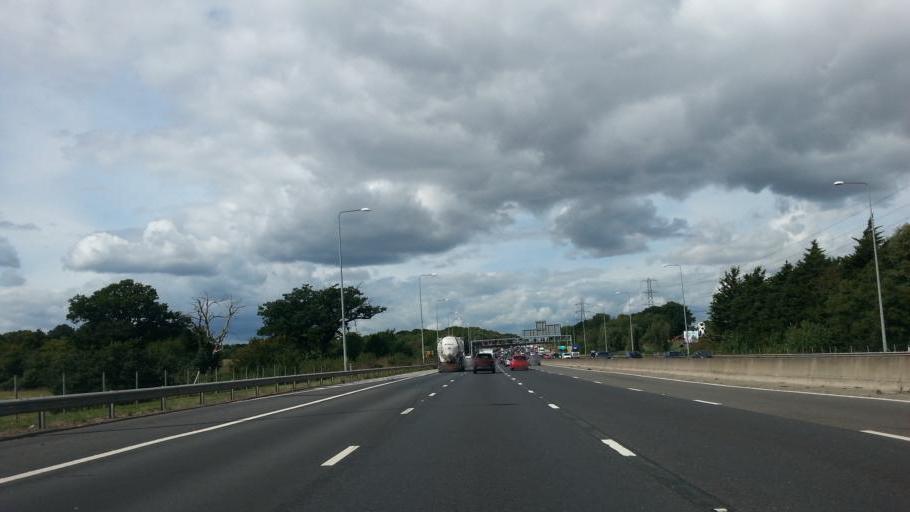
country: GB
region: England
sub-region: Greater London
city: Harold Wood
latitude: 51.6231
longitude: 0.2388
